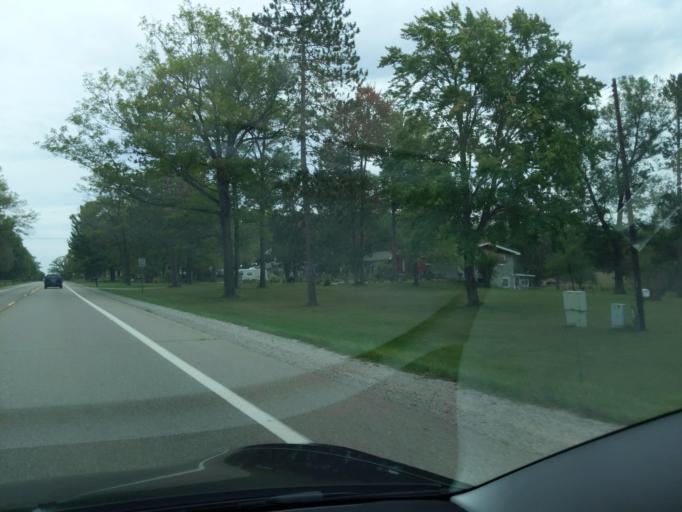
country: US
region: Michigan
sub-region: Clare County
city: Clare
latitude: 43.8493
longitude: -84.8919
